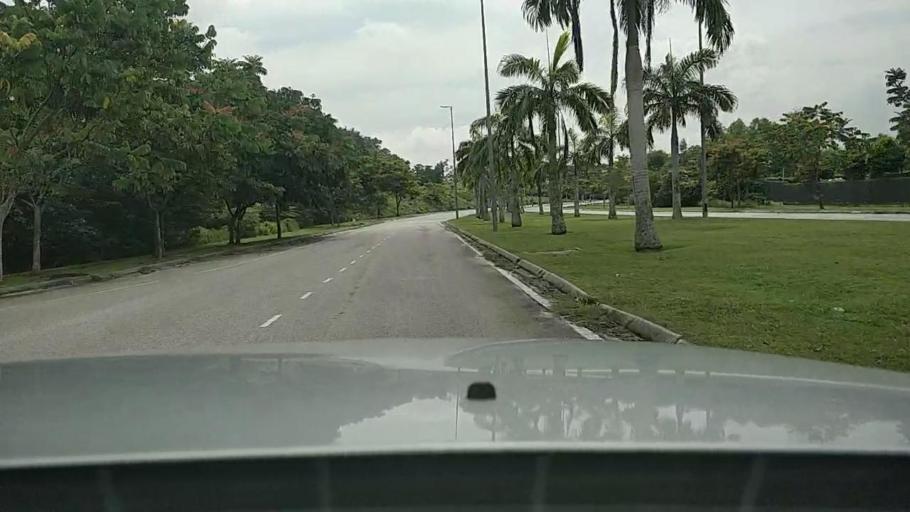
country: MY
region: Putrajaya
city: Putrajaya
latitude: 2.9046
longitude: 101.6525
